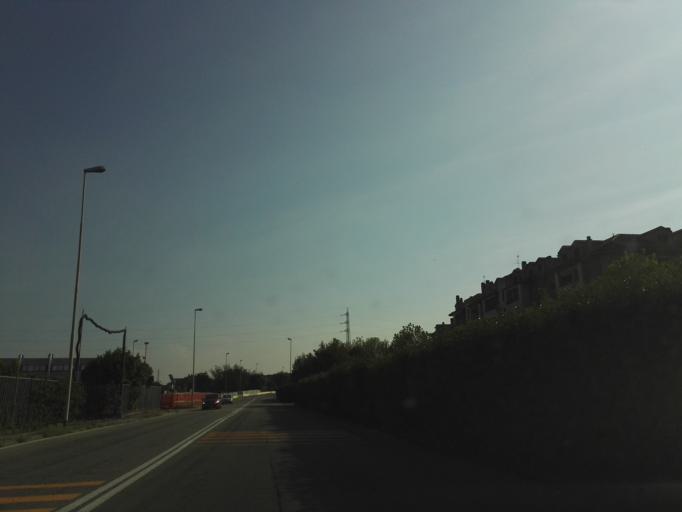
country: IT
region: Lombardy
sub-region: Citta metropolitana di Milano
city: Triginto
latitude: 45.3879
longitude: 9.3084
